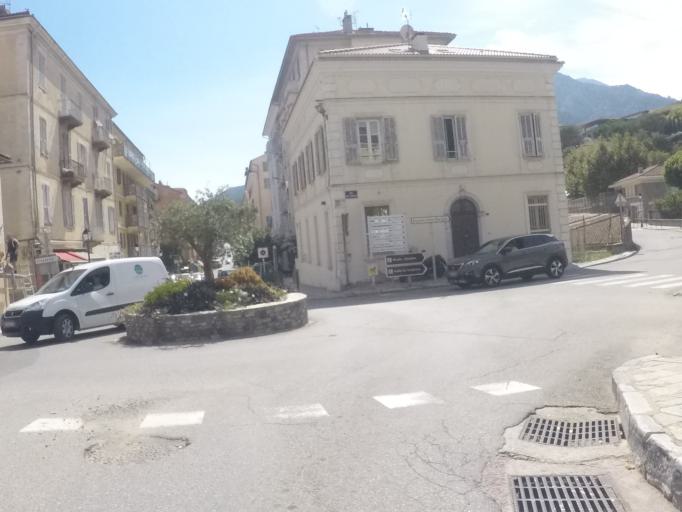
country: FR
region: Corsica
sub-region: Departement de la Haute-Corse
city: Corte
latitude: 42.3092
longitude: 9.1498
